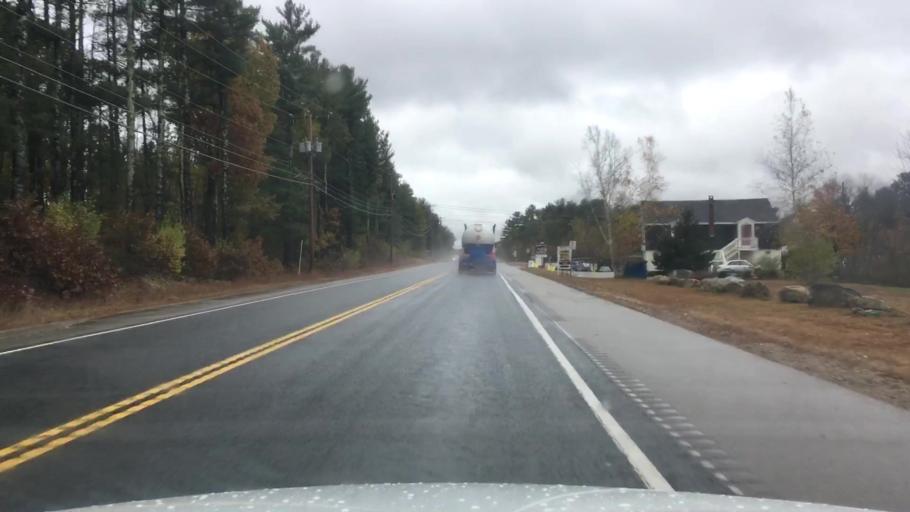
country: US
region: New Hampshire
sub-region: Strafford County
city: Barrington
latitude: 43.1973
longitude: -70.9977
